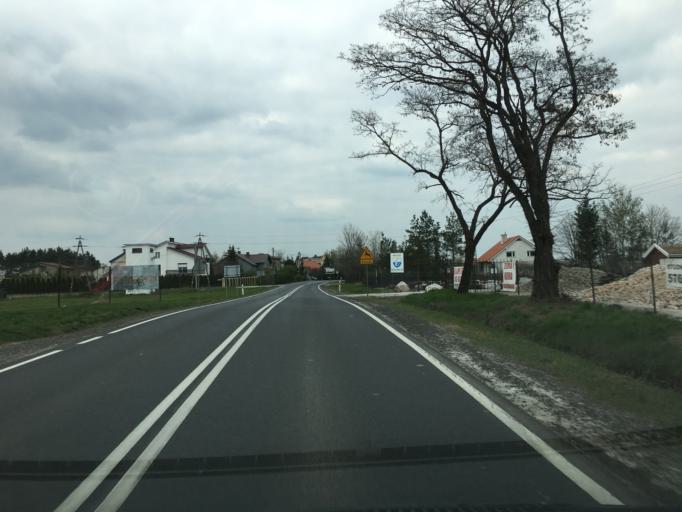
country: PL
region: Lower Silesian Voivodeship
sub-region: Powiat legnicki
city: Prochowice
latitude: 51.2685
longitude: 16.3478
